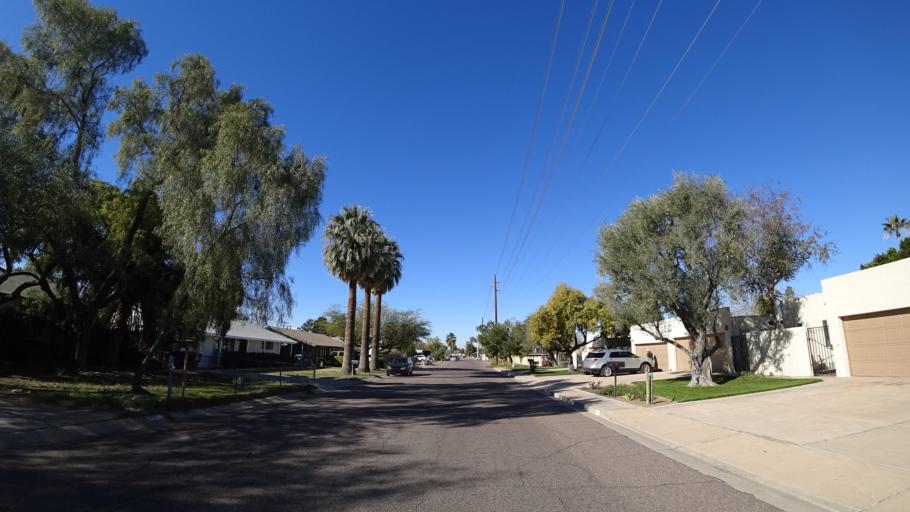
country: US
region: Arizona
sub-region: Maricopa County
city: Paradise Valley
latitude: 33.4783
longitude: -111.9668
